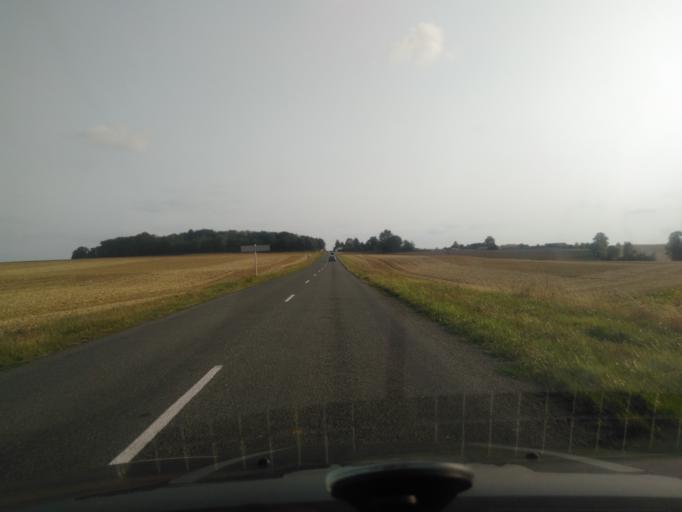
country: FR
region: Picardie
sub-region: Departement de l'Aisne
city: Bruyeres-et-Montberault
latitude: 49.5060
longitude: 3.6734
